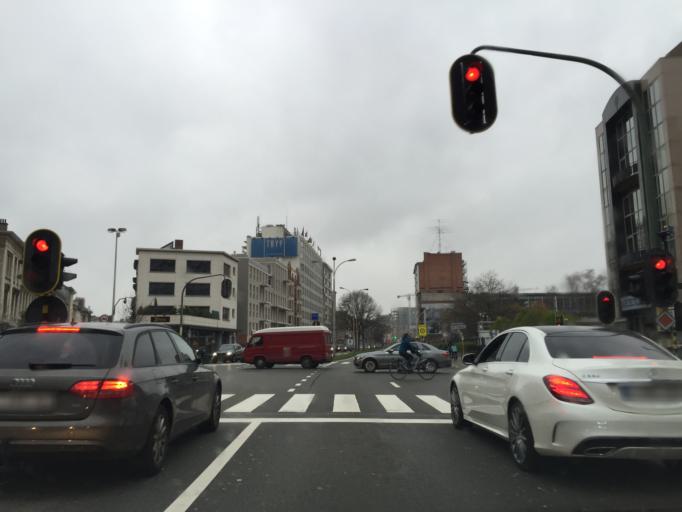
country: BE
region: Flanders
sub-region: Provincie Antwerpen
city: Antwerpen
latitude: 51.2092
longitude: 4.4326
